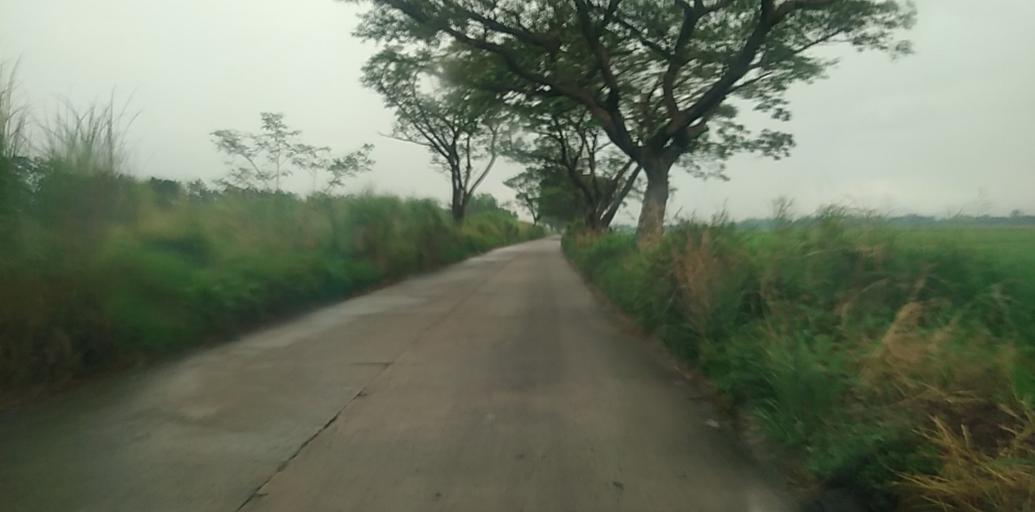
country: PH
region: Central Luzon
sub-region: Province of Pampanga
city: San Antonio
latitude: 15.1550
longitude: 120.6973
